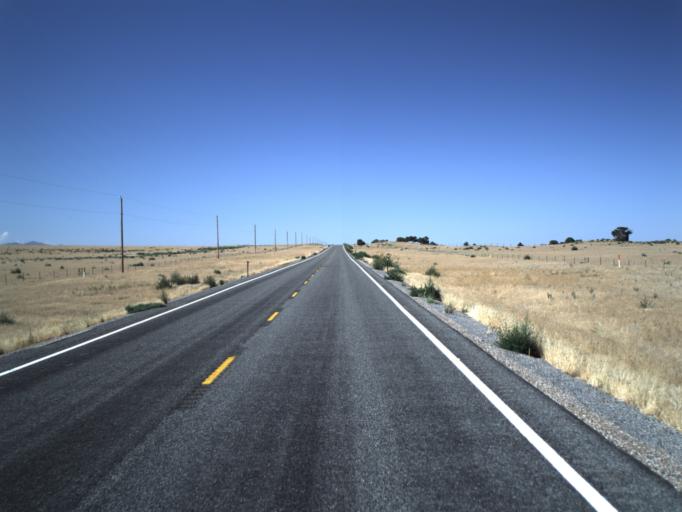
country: US
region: Utah
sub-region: Millard County
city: Delta
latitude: 39.6357
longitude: -112.3069
